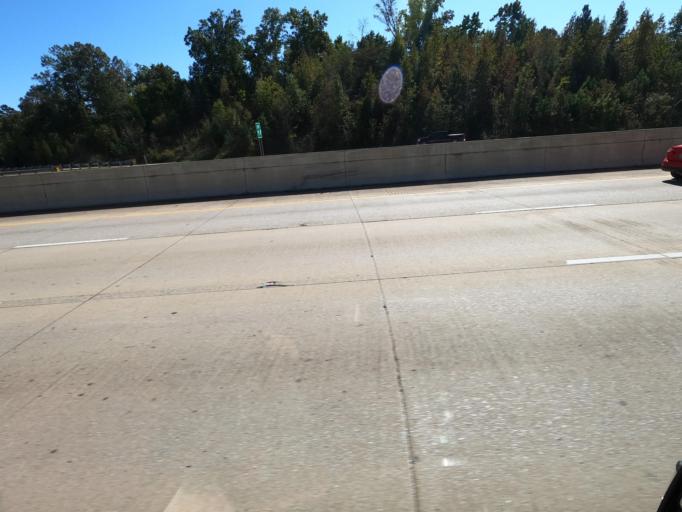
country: US
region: Tennessee
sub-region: Hamilton County
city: Harrison
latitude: 35.0722
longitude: -85.1162
